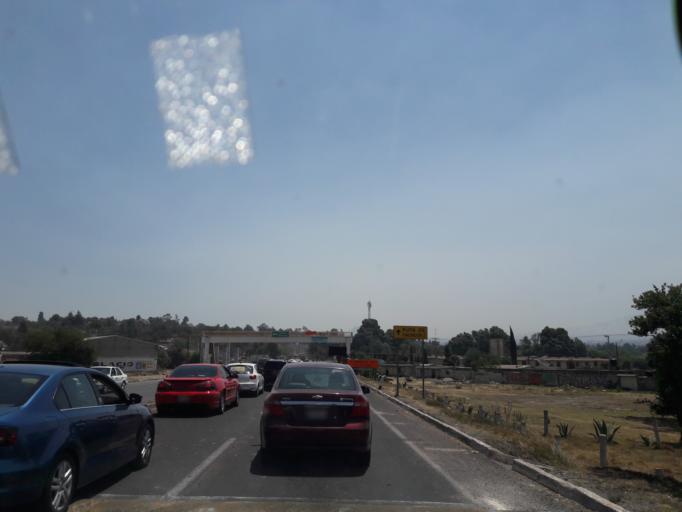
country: MX
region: Tlaxcala
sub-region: Apetatitlan de Antonio Carvajal
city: Tlatempan
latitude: 19.3427
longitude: -98.2027
